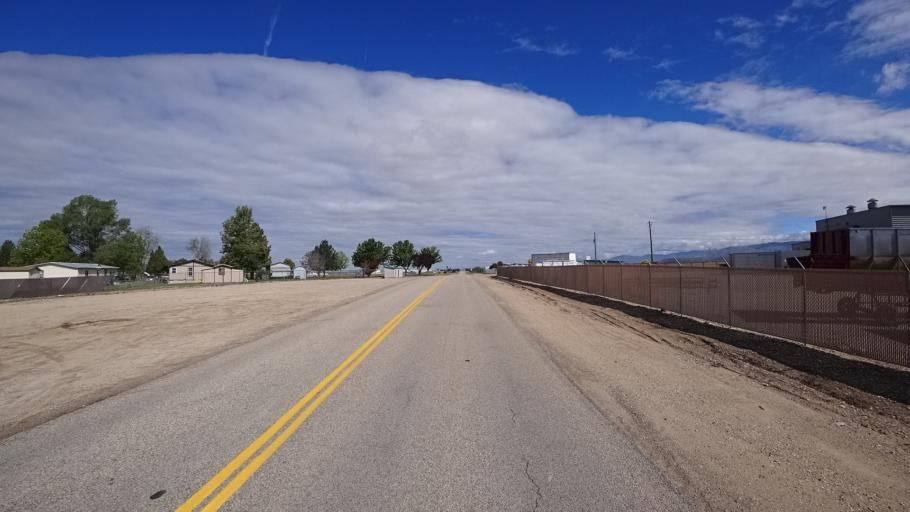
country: US
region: Idaho
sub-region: Ada County
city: Boise
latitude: 43.5270
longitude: -116.1552
